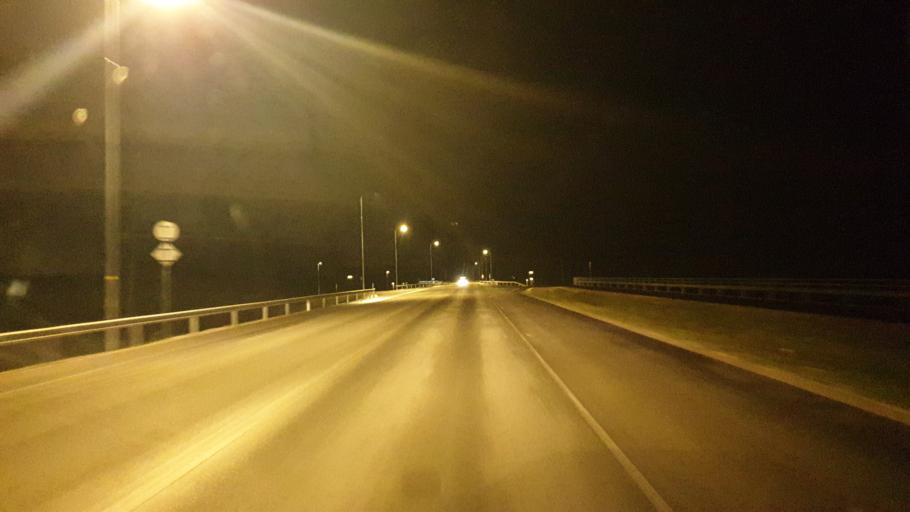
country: FI
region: Central Finland
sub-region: Jyvaeskylae
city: Jyvaeskylae
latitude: 62.3529
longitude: 25.7060
